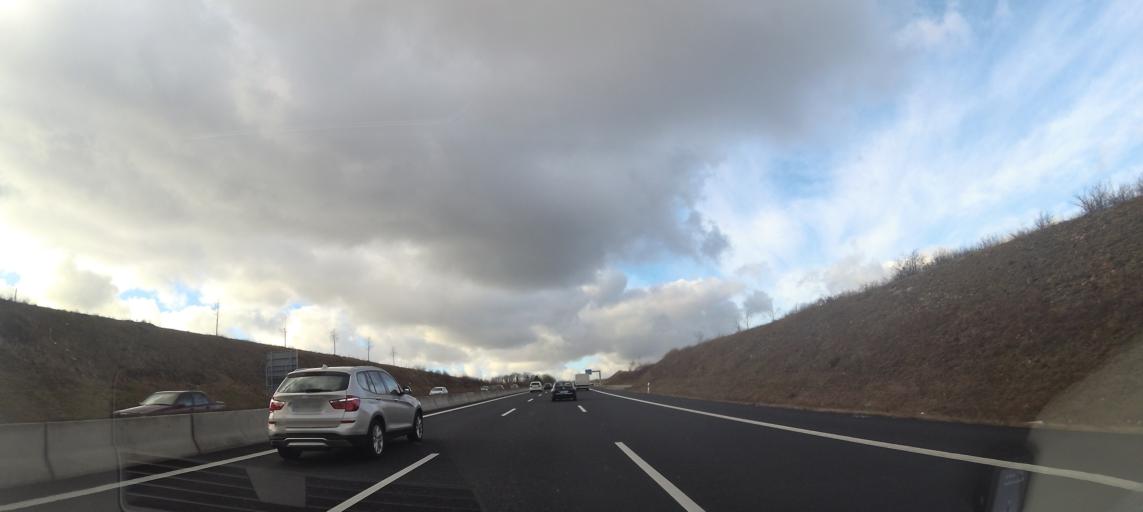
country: DE
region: Baden-Wuerttemberg
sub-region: Regierungsbezirk Stuttgart
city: Rutesheim
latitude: 48.8028
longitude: 8.9391
